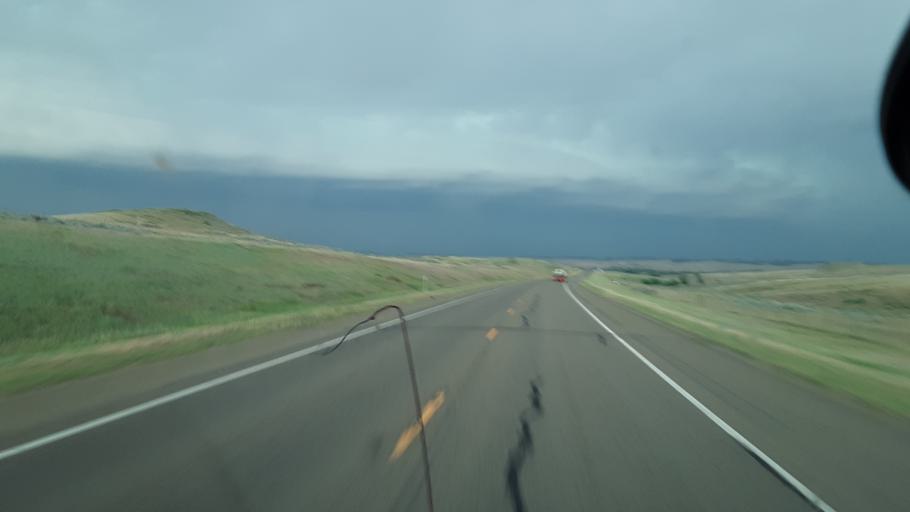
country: US
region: Montana
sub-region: Powder River County
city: Broadus
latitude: 45.4066
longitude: -105.3749
